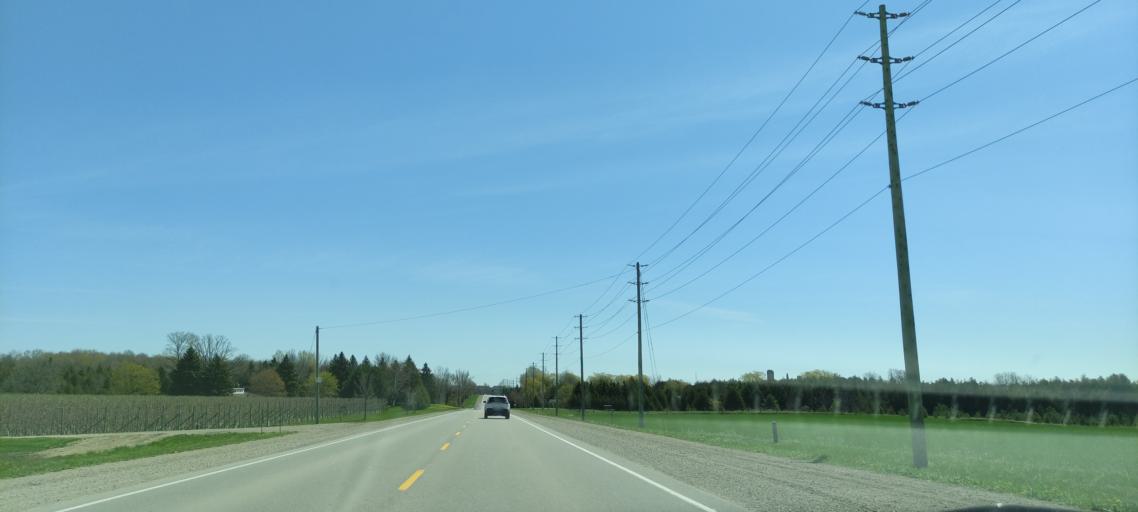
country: CA
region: Ontario
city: Waterloo
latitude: 43.5945
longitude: -80.5009
